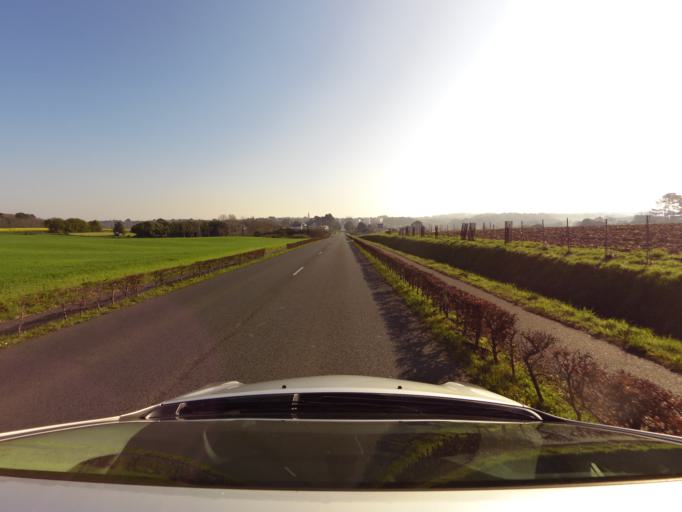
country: FR
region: Brittany
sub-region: Departement du Morbihan
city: Guidel-Plage
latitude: 47.7796
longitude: -3.5072
